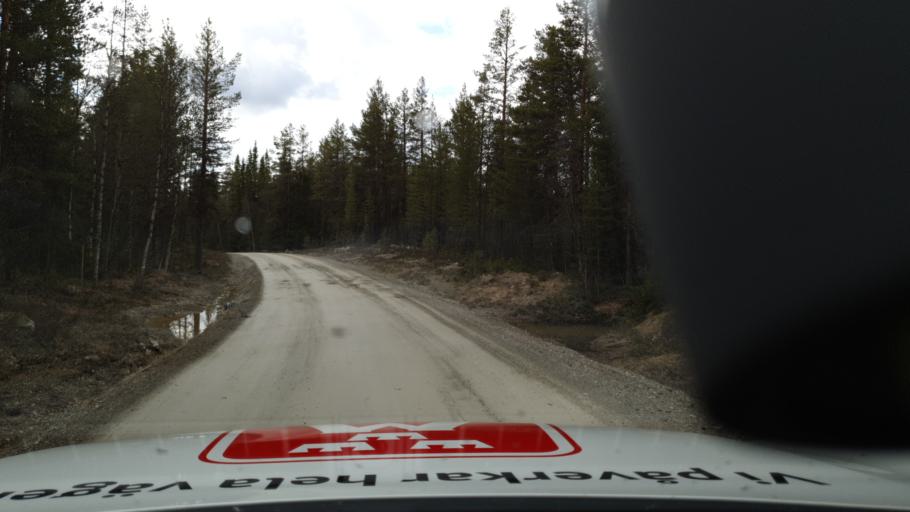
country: SE
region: Jaemtland
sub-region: Bergs Kommun
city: Hoverberg
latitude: 62.7668
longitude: 13.8241
